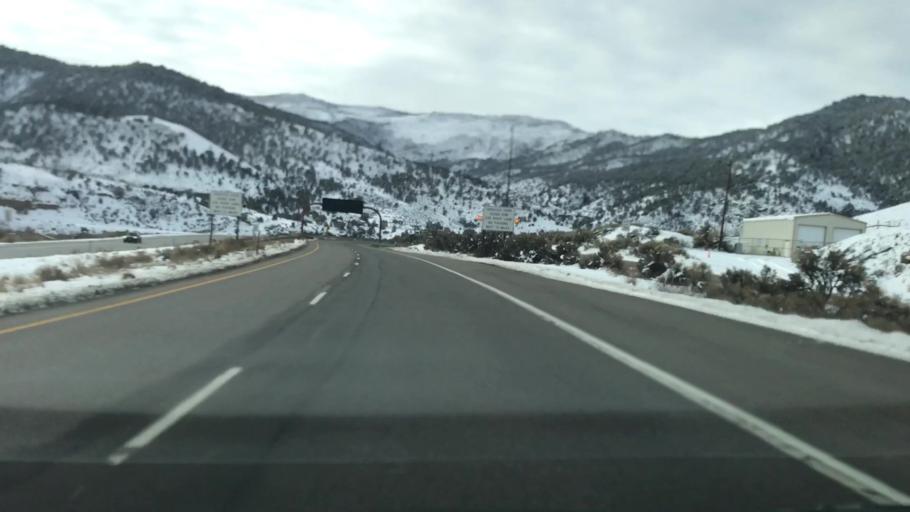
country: US
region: Colorado
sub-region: Eagle County
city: Gypsum
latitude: 39.6298
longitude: -107.1036
